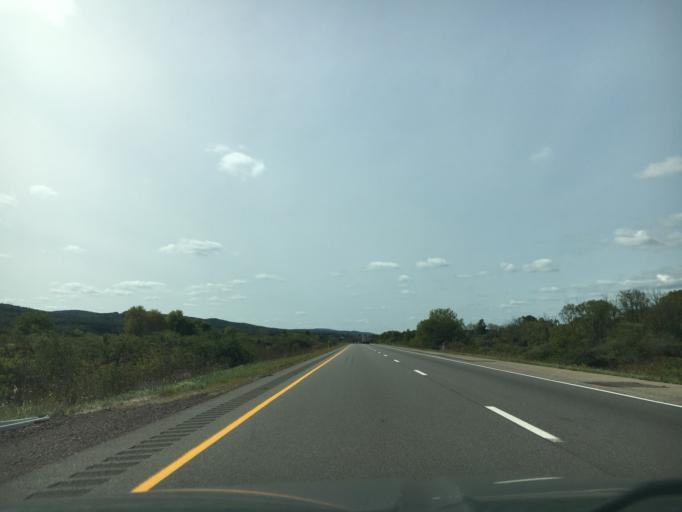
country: US
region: Pennsylvania
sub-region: Montour County
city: Mechanicsville
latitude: 41.0060
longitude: -76.5577
